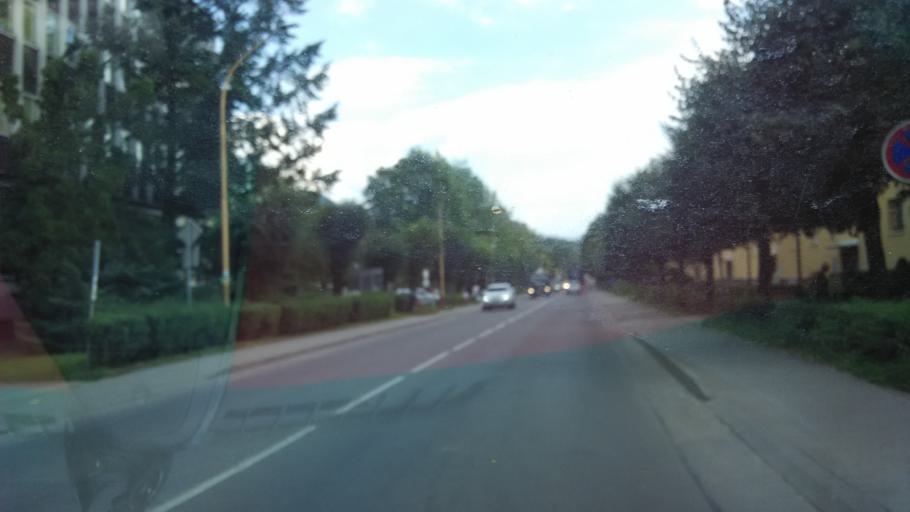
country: SK
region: Zilinsky
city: Kysucke Nove Mesto
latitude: 49.2999
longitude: 18.7837
